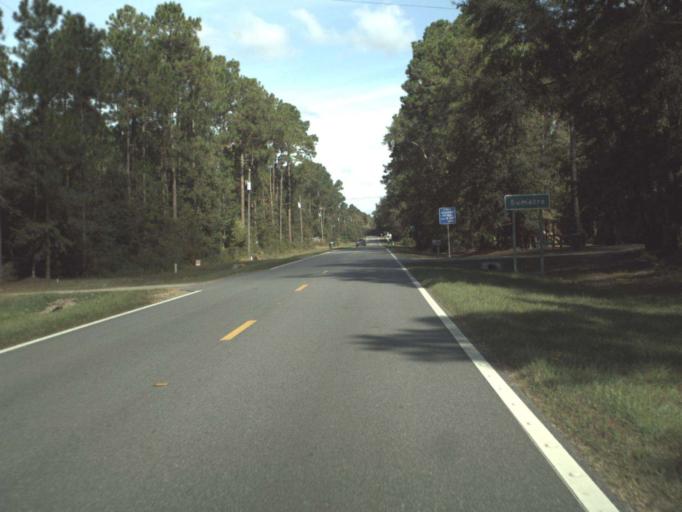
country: US
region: Florida
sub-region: Gulf County
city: Wewahitchka
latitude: 30.0141
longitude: -84.9790
